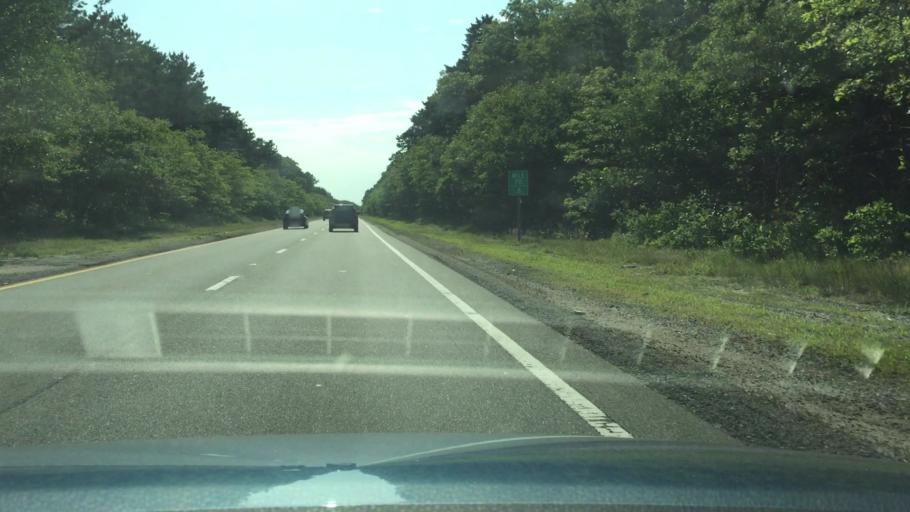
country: US
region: Massachusetts
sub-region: Barnstable County
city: Barnstable
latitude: 41.6876
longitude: -70.2866
